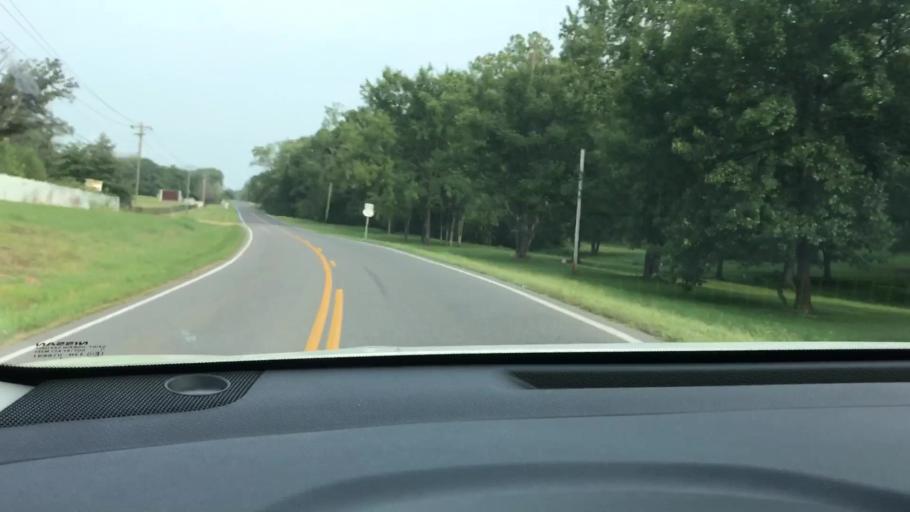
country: US
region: Kentucky
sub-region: Calloway County
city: Murray
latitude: 36.5852
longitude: -88.2935
